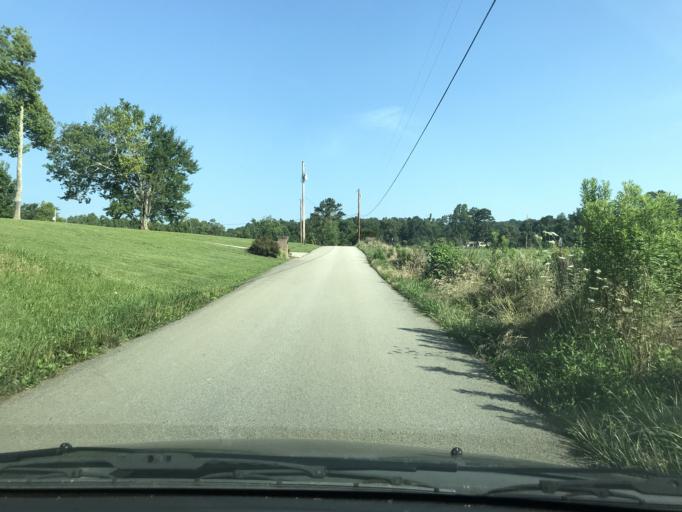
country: US
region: Tennessee
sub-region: Loudon County
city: Loudon
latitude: 35.8142
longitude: -84.3440
